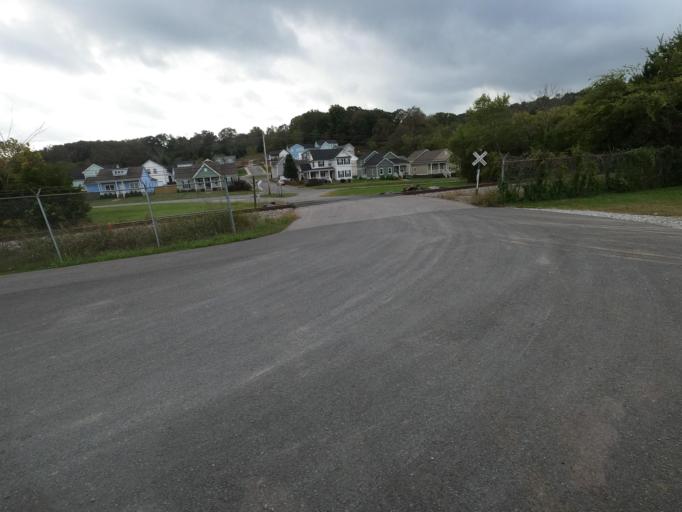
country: US
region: Tennessee
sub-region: Cheatham County
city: Kingston Springs
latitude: 36.1022
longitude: -87.1185
